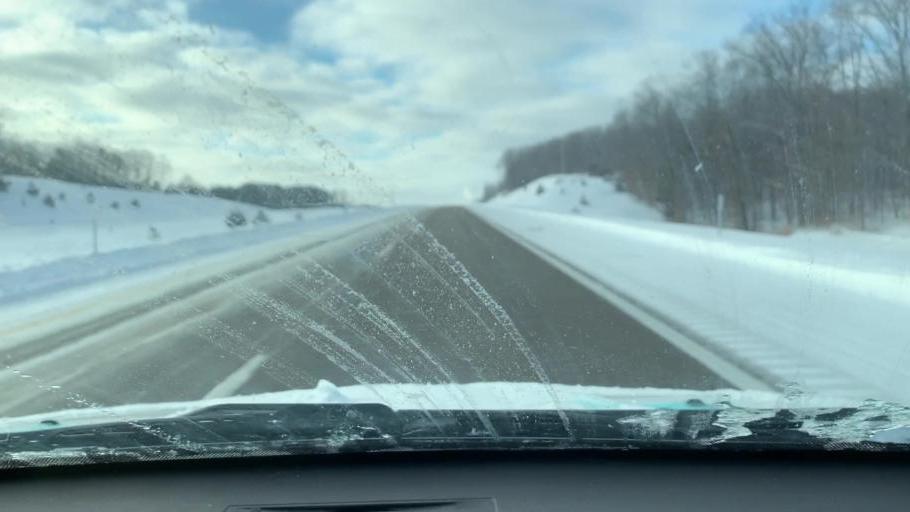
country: US
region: Michigan
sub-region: Wexford County
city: Manton
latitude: 44.3532
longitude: -85.4041
